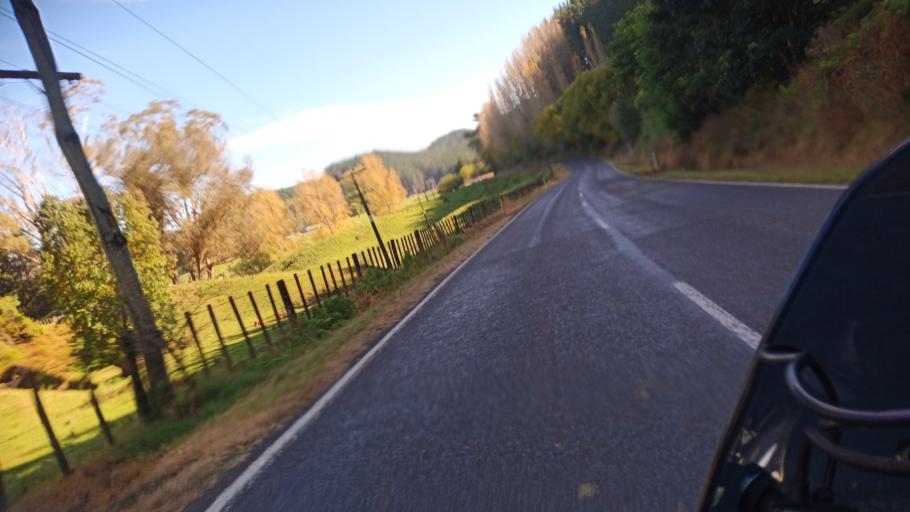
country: NZ
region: Hawke's Bay
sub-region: Wairoa District
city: Wairoa
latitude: -38.9249
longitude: 177.2722
